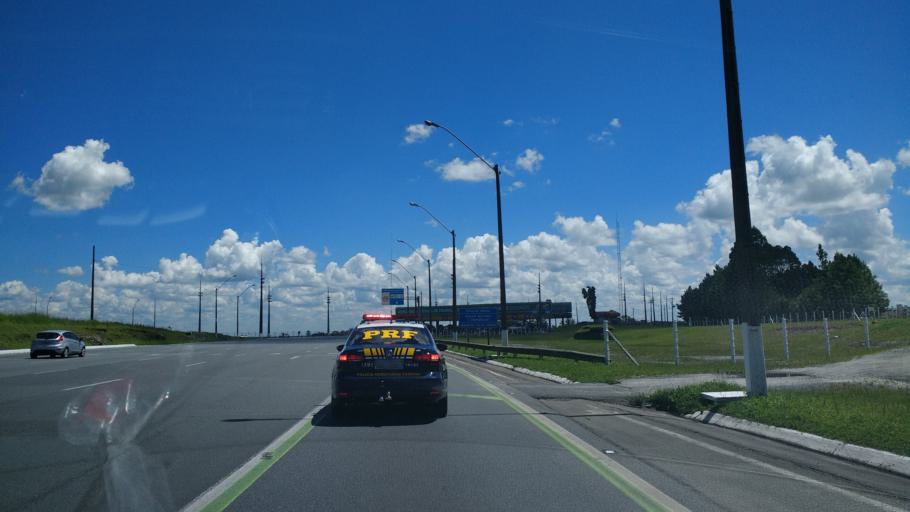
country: BR
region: Parana
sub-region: Campo Largo
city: Campo Largo
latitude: -25.4699
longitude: -49.6596
